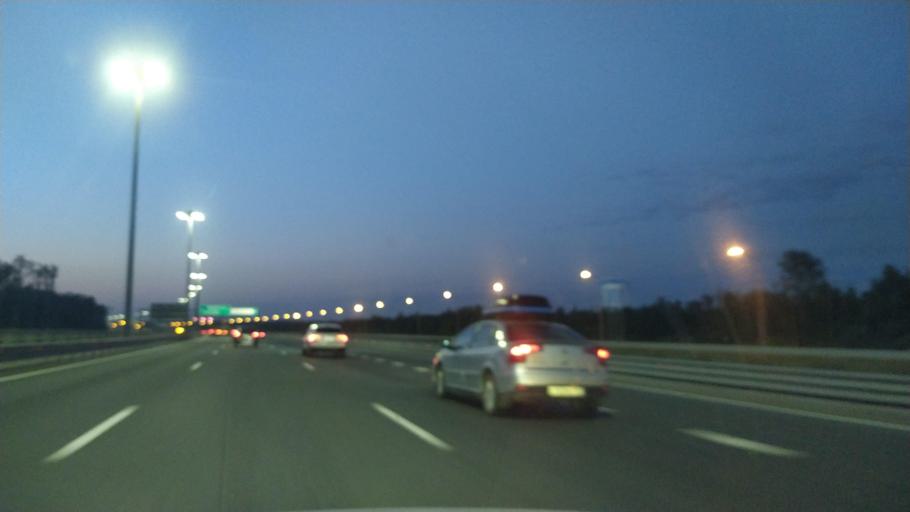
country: RU
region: St.-Petersburg
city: Levashovo
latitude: 60.0643
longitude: 30.1645
